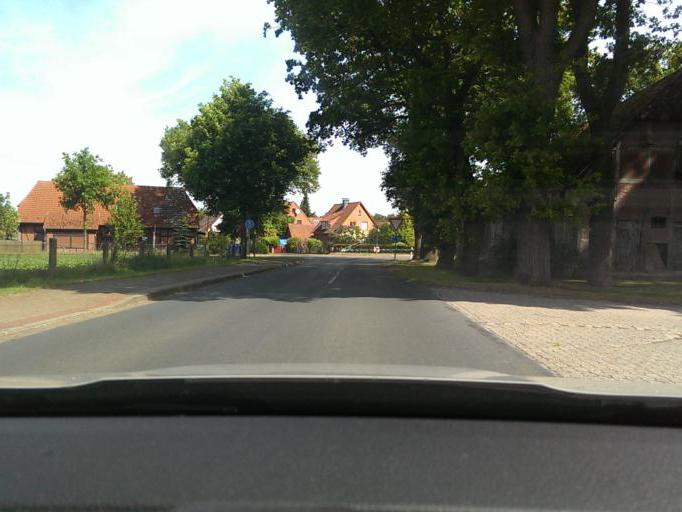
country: DE
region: Lower Saxony
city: Essel
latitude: 52.6746
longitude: 9.6749
